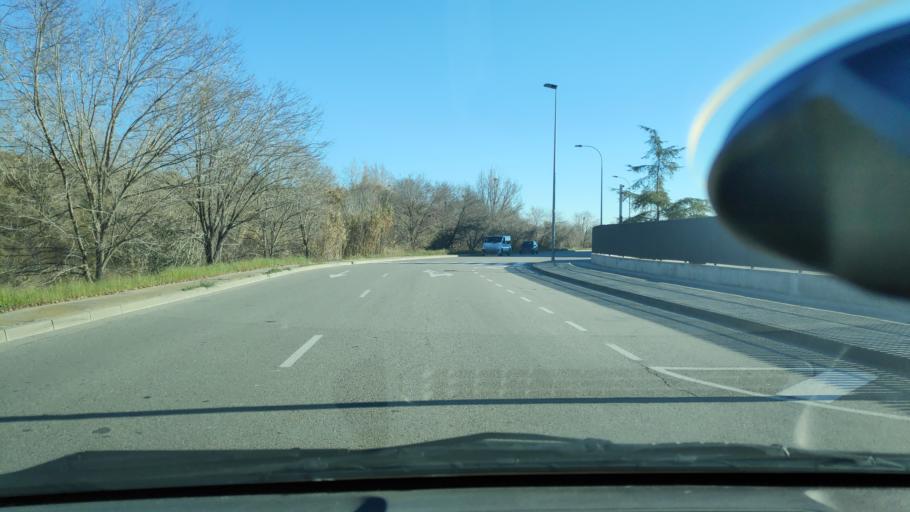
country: ES
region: Catalonia
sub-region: Provincia de Barcelona
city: Sant Quirze del Valles
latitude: 41.5249
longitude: 2.0927
